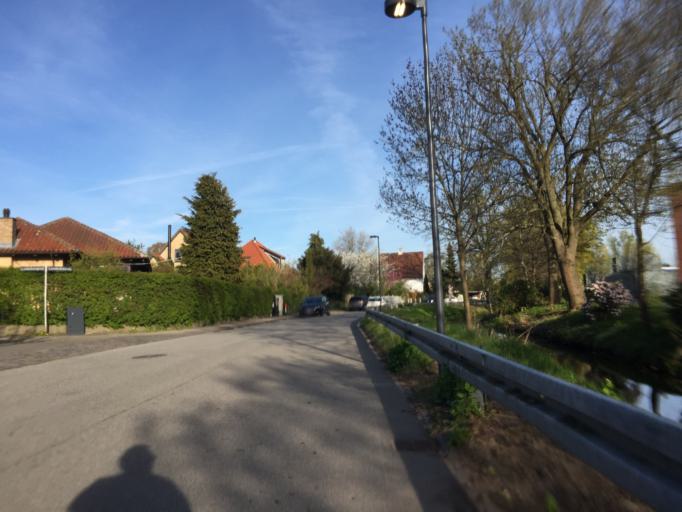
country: DK
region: Capital Region
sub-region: Frederiksberg Kommune
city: Frederiksberg
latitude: 55.7236
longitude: 12.5439
